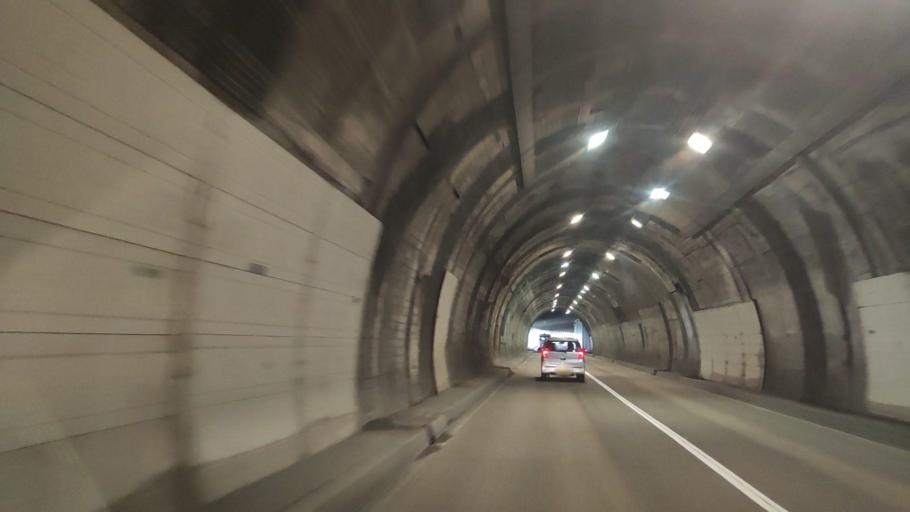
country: JP
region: Hokkaido
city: Date
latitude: 42.5639
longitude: 140.7394
